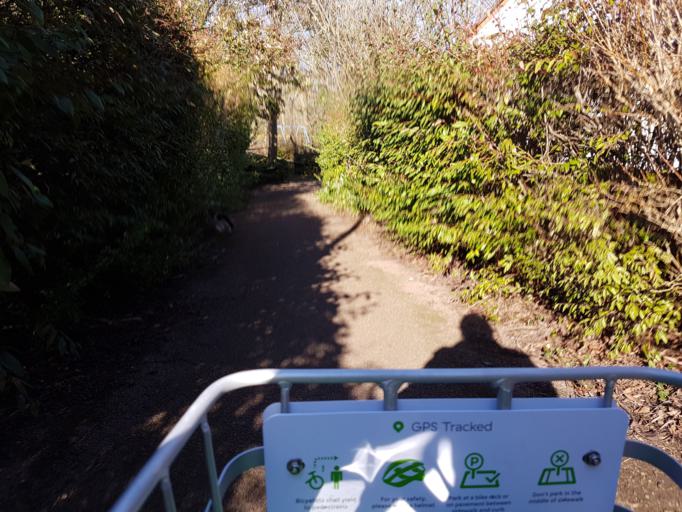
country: GB
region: England
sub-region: Buckinghamshire
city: Newton Longville
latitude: 52.0036
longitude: -0.7674
